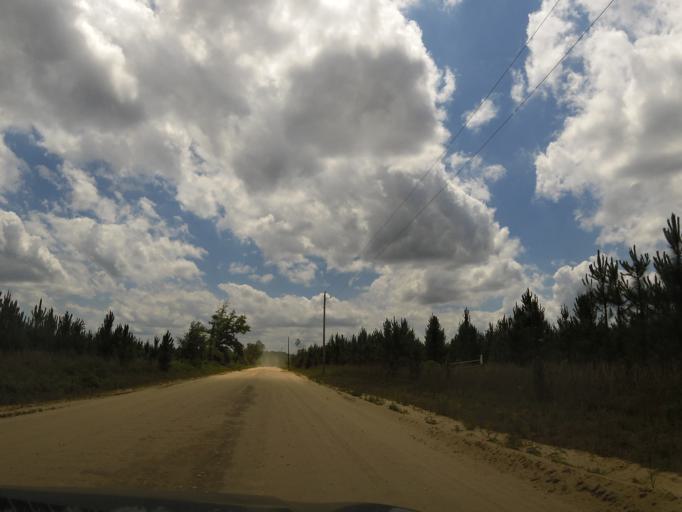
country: US
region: Florida
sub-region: Clay County
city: Asbury Lake
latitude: 29.9087
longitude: -81.8007
